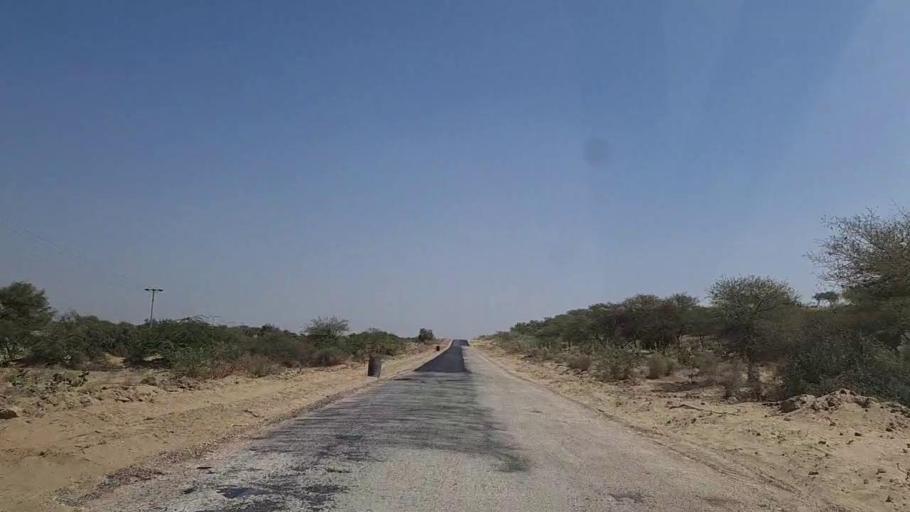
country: PK
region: Sindh
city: Diplo
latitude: 24.4792
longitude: 69.5133
